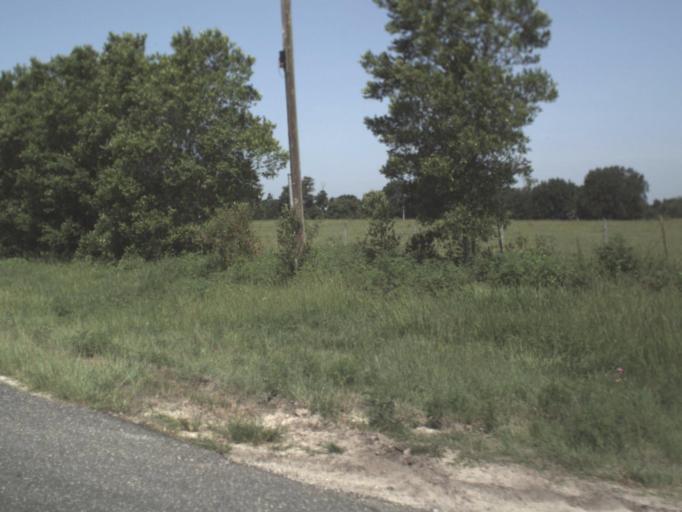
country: US
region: Florida
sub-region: Levy County
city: Chiefland
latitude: 29.4994
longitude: -82.8393
